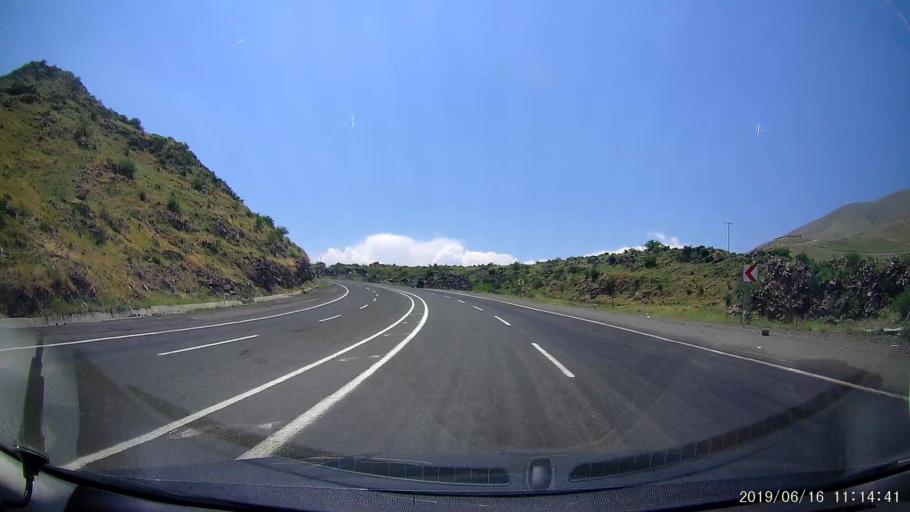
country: TR
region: Igdir
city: Igdir
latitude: 39.7748
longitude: 44.1413
